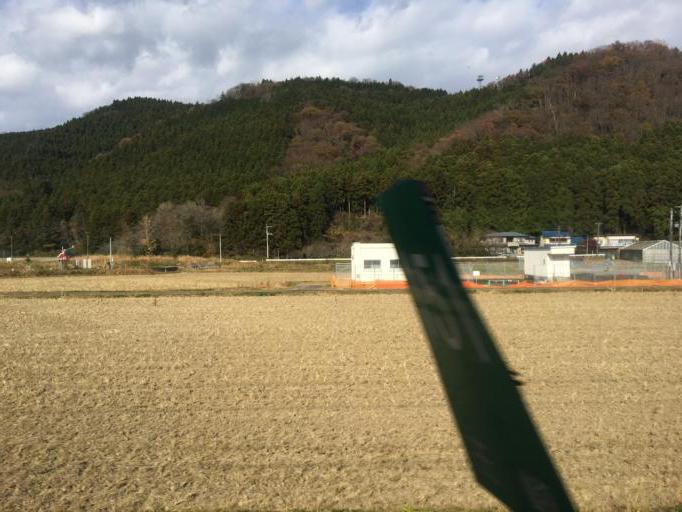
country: JP
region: Miyagi
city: Iwanuma
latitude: 38.0886
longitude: 140.8346
